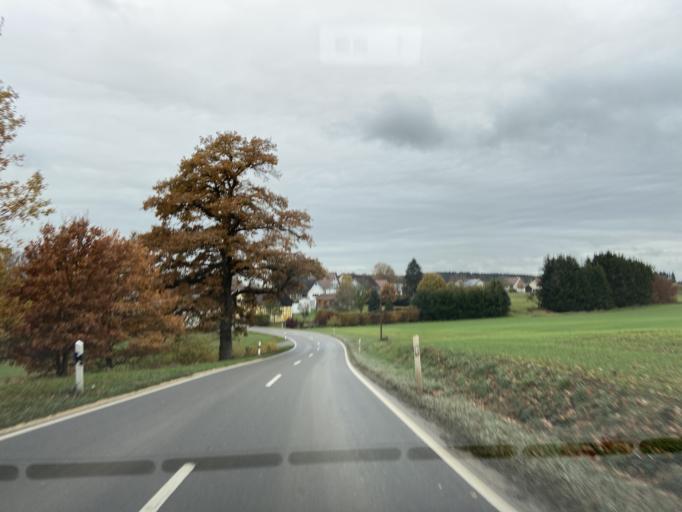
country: DE
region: Baden-Wuerttemberg
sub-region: Tuebingen Region
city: Wald
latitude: 47.9645
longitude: 9.2101
